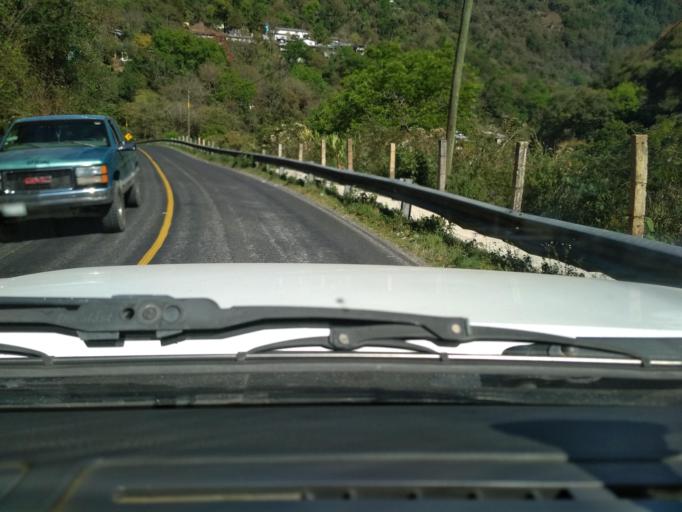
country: MX
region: Veracruz
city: Tequila
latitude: 18.7491
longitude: -97.0901
